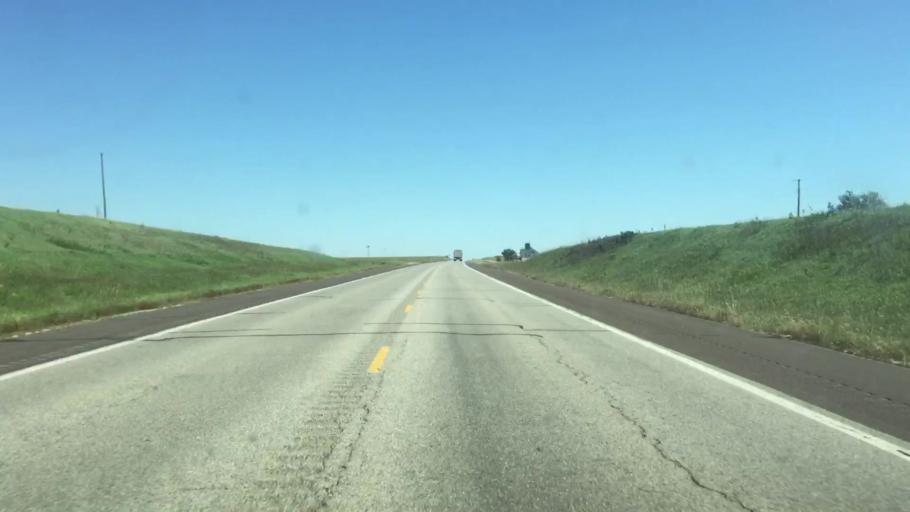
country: US
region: Kansas
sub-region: Nemaha County
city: Seneca
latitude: 39.8421
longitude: -96.2784
